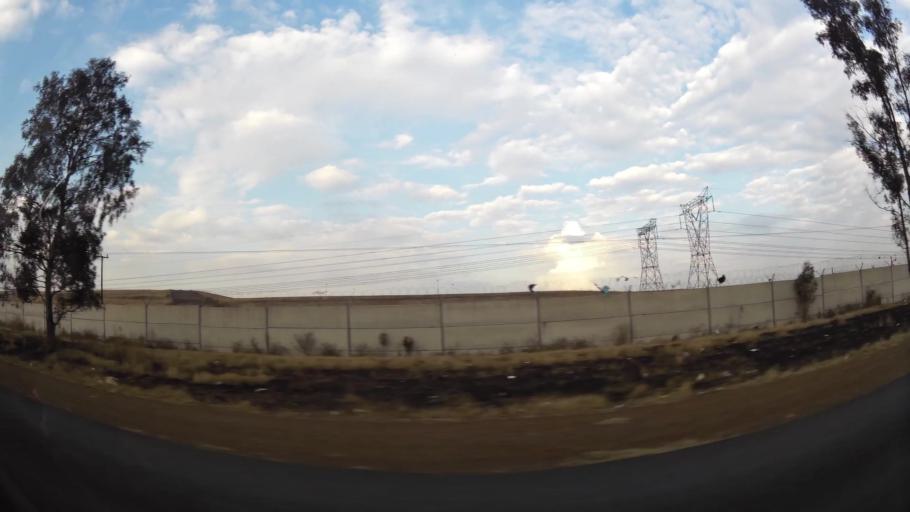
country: ZA
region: Gauteng
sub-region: Sedibeng District Municipality
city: Vanderbijlpark
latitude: -26.6413
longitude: 27.8056
